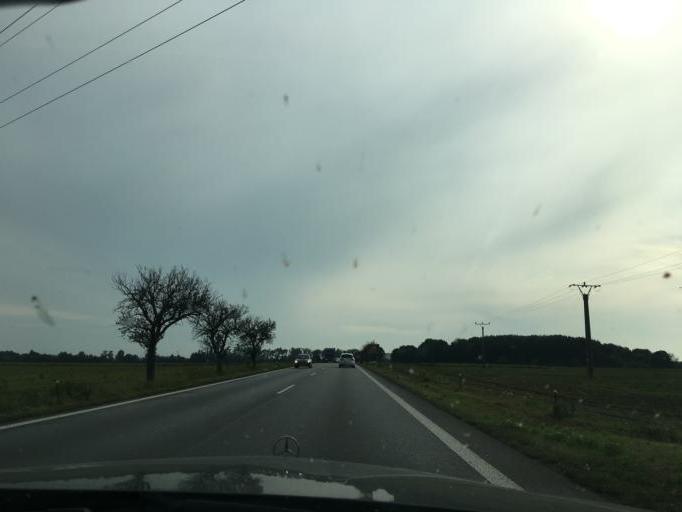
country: CZ
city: Predmerice nad Labem
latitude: 50.2507
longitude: 15.8013
